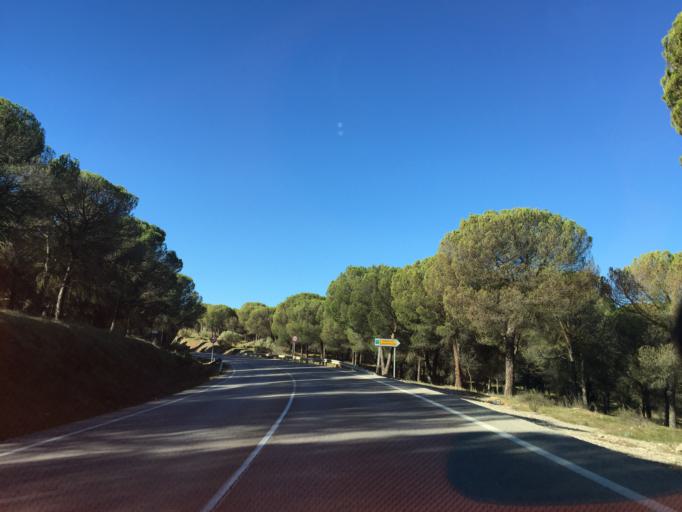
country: ES
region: Andalusia
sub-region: Provincia de Malaga
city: Ronda
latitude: 36.7576
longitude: -5.1674
